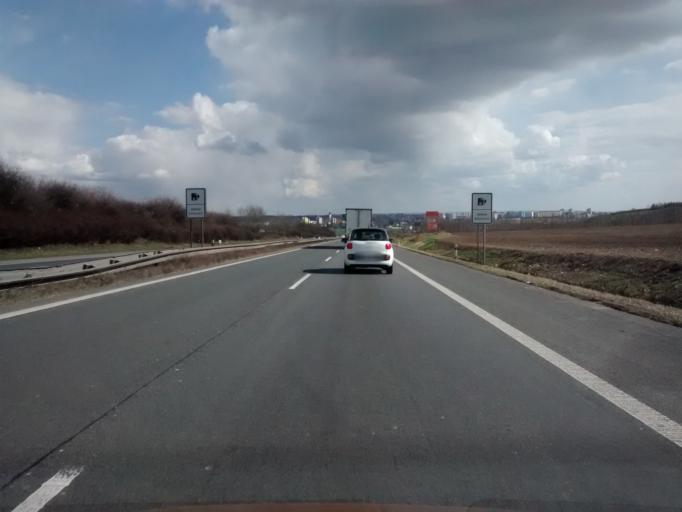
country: CZ
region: Central Bohemia
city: Zdiby
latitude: 50.1623
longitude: 14.4754
